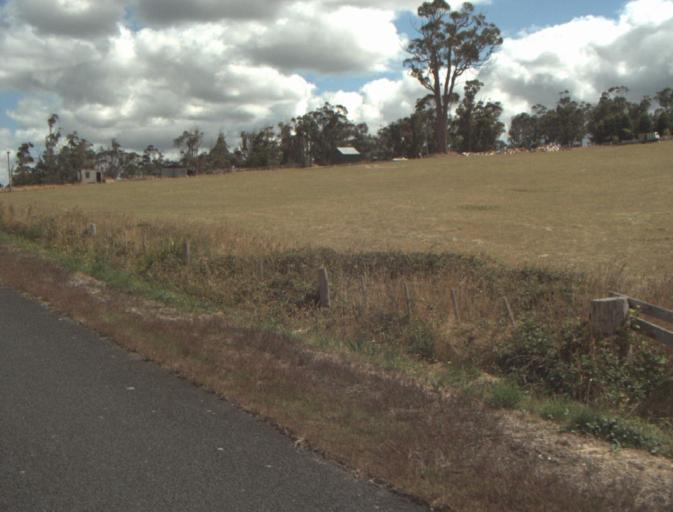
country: AU
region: Tasmania
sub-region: Launceston
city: Mayfield
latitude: -41.2061
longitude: 147.0968
